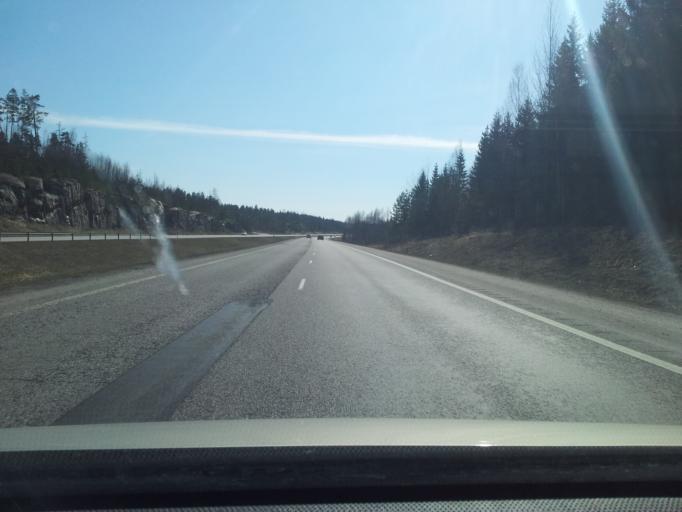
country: FI
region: Uusimaa
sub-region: Porvoo
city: Porvoo
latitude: 60.4555
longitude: 25.8405
